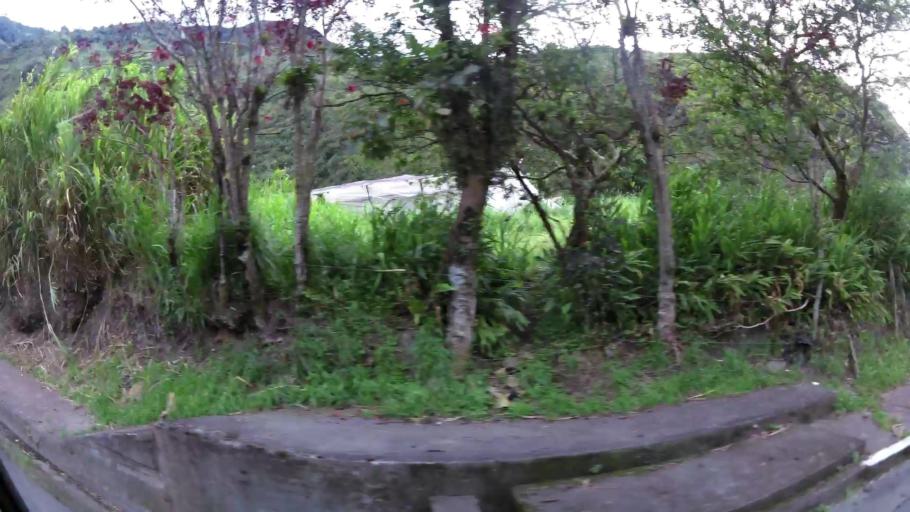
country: EC
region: Tungurahua
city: Banos
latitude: -1.3967
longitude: -78.3866
